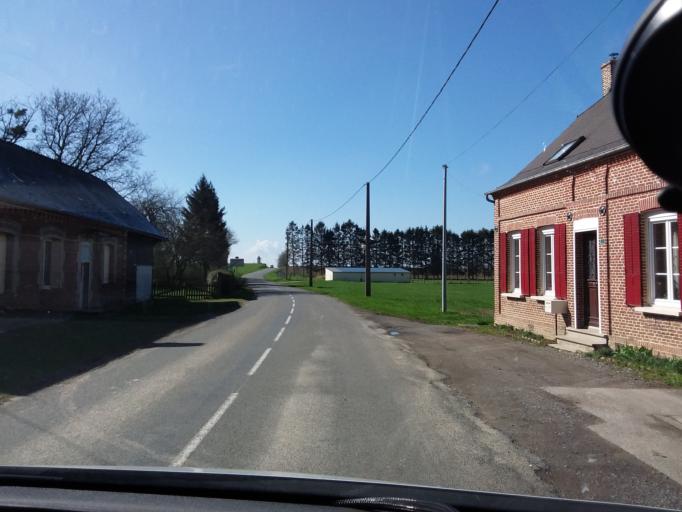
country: FR
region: Picardie
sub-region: Departement de l'Aisne
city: Montcornet
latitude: 49.7478
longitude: 3.9984
